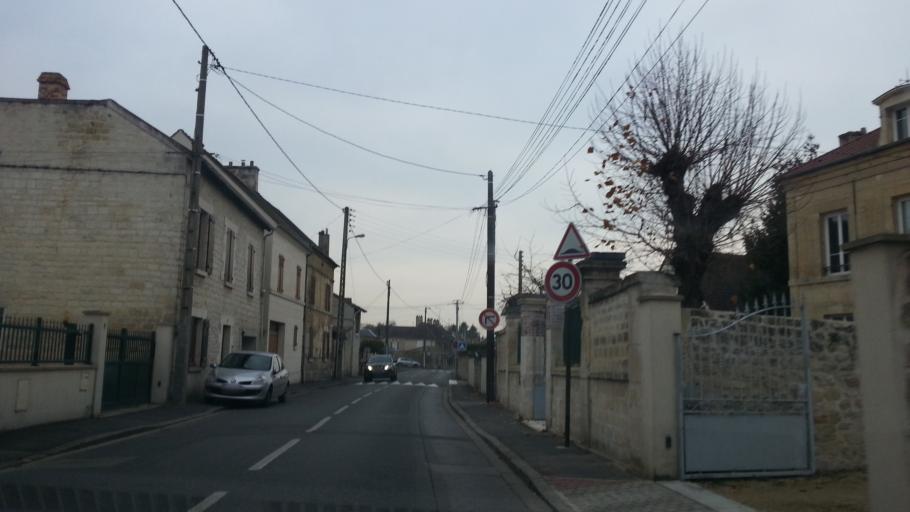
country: FR
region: Picardie
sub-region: Departement de l'Oise
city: Gouvieux
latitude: 49.1848
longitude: 2.4107
